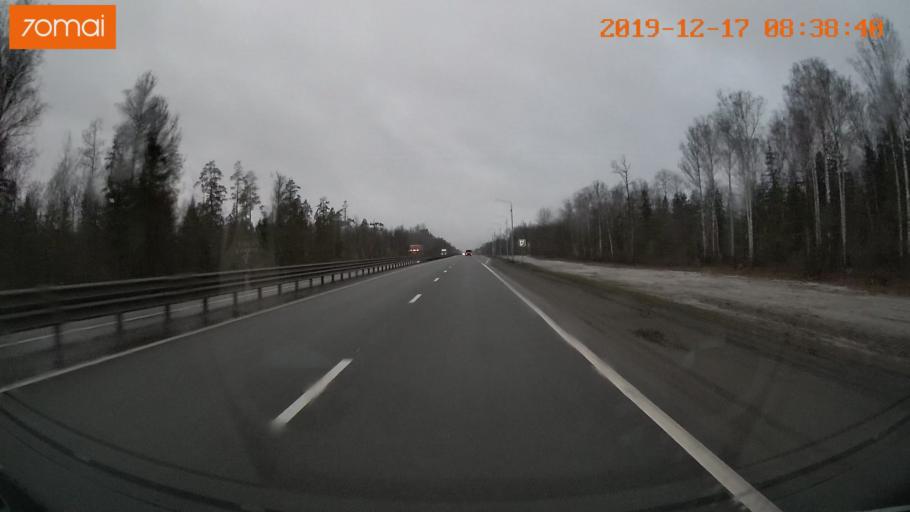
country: RU
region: Vladimir
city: Lakinsk
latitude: 55.9791
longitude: 39.8282
